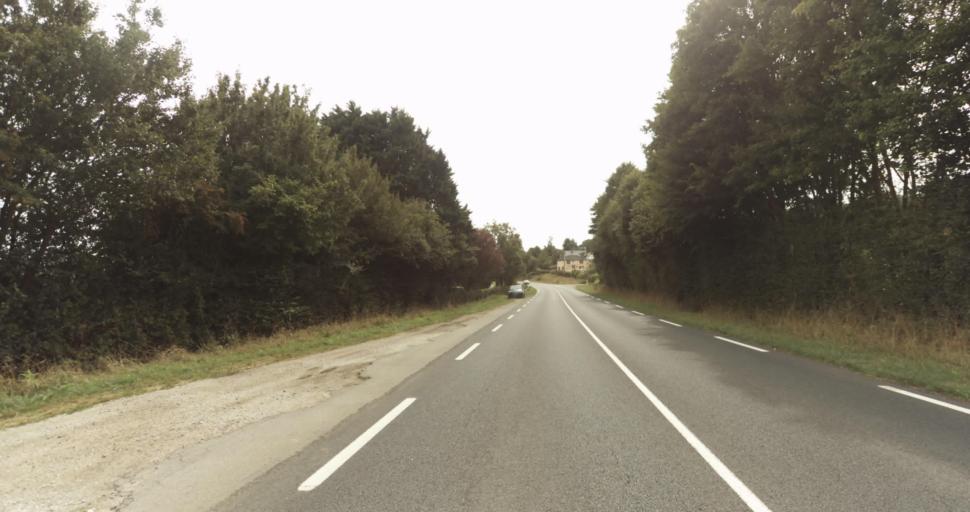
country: FR
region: Lower Normandy
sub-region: Departement de l'Orne
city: Gace
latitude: 48.8179
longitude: 0.2808
